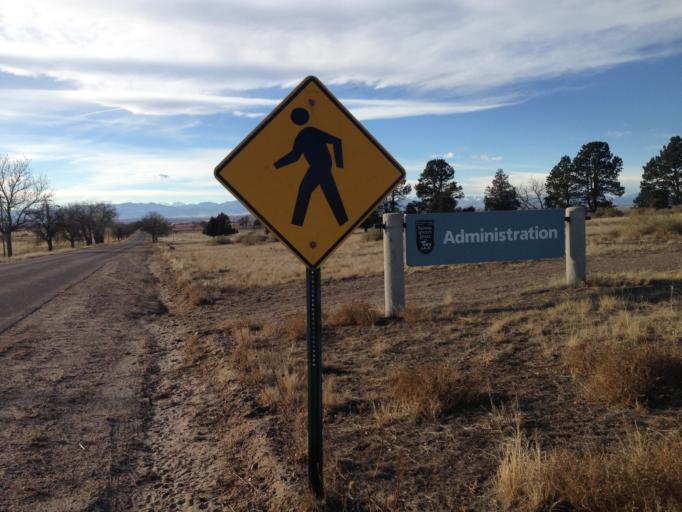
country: US
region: Colorado
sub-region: Adams County
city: Derby
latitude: 39.8273
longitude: -104.8587
